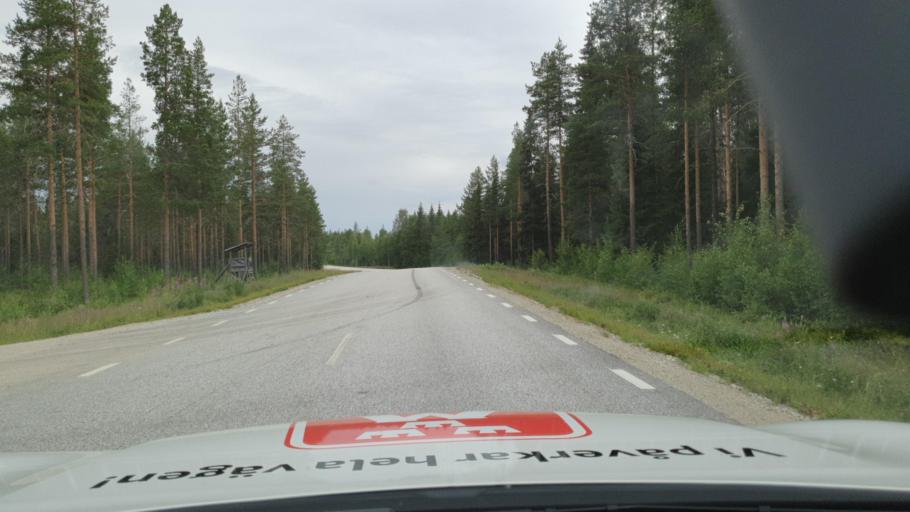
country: SE
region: Vaesterbotten
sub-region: Bjurholms Kommun
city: Bjurholm
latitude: 64.1550
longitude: 19.3565
